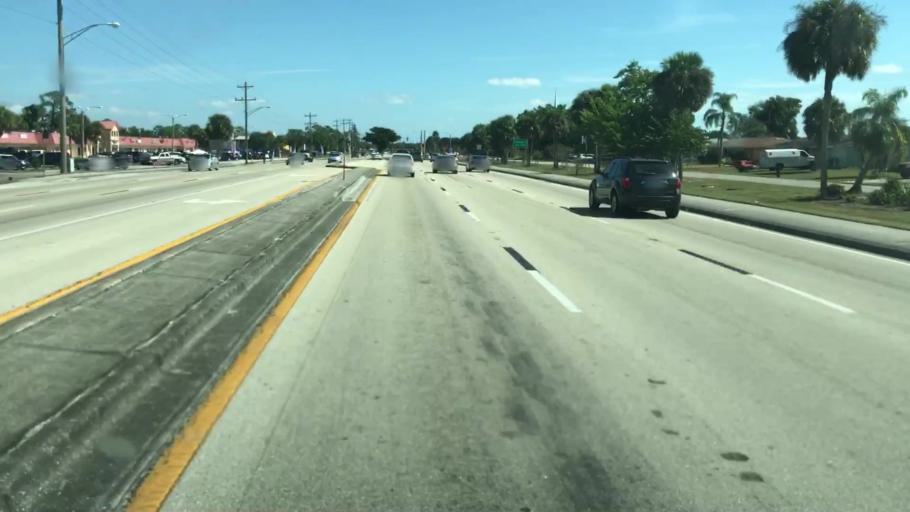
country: US
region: Florida
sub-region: Lee County
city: Lehigh Acres
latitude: 26.6142
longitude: -81.6579
